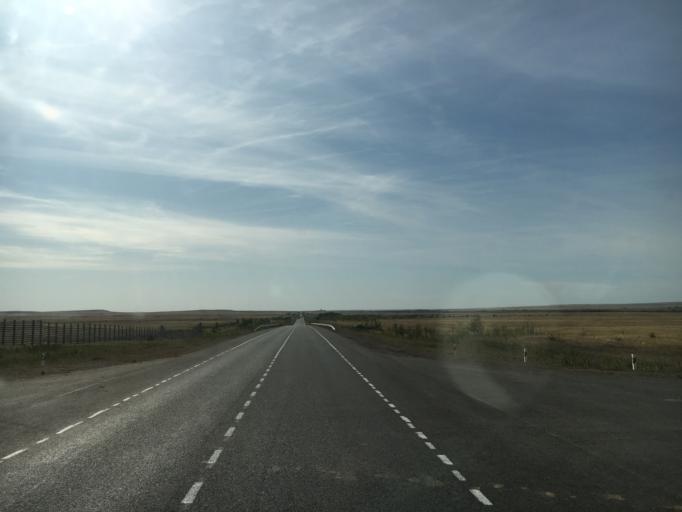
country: KZ
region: Batys Qazaqstan
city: Kamenka
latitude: 51.1083
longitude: 50.4370
